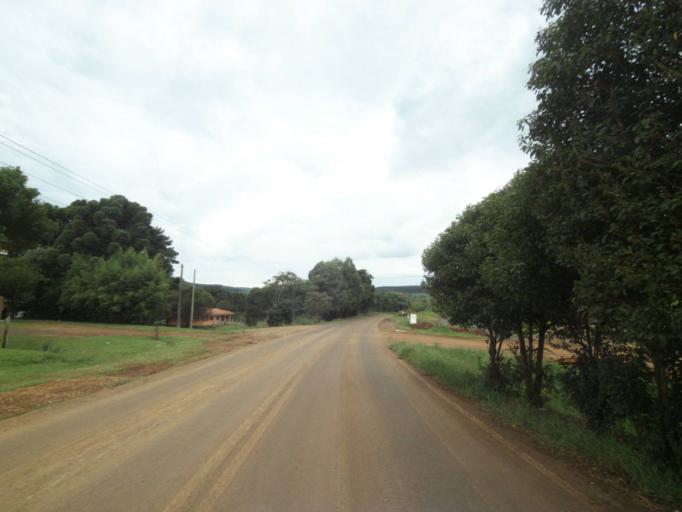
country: BR
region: Parana
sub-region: Pitanga
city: Pitanga
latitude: -24.8948
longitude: -51.9599
